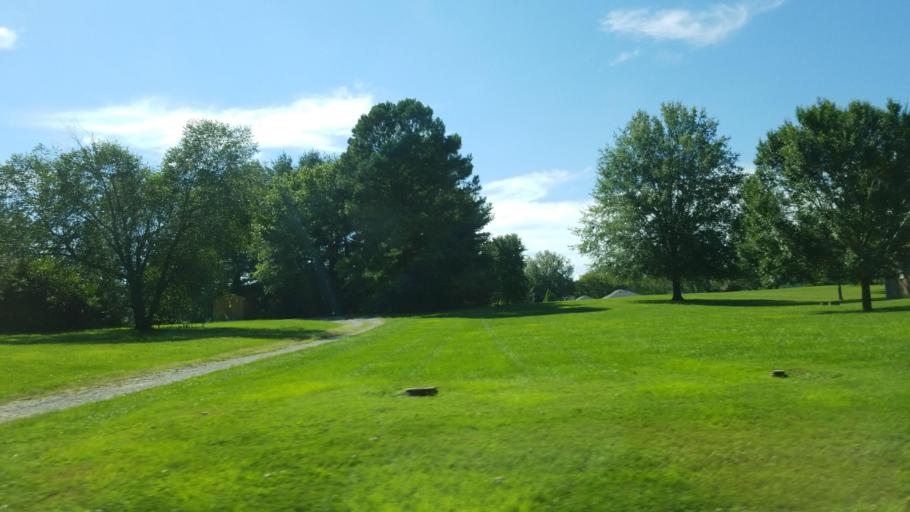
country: US
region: Illinois
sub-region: Williamson County
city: Marion
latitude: 37.7475
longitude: -88.8785
